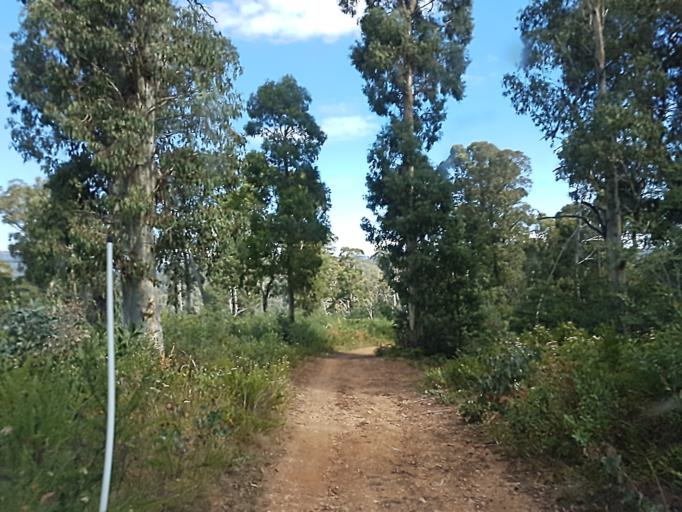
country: AU
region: Victoria
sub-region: Alpine
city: Mount Beauty
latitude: -36.9194
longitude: 146.9972
